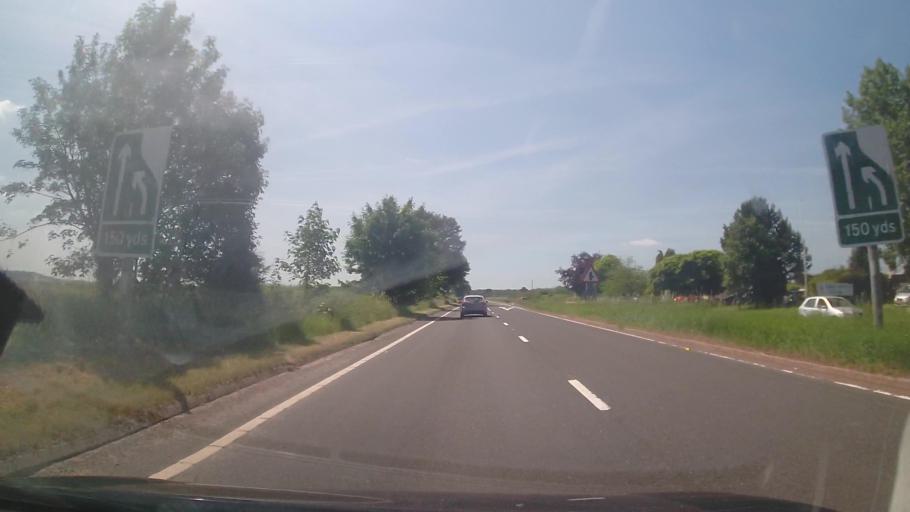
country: GB
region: England
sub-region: Herefordshire
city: Wellington
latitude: 52.1332
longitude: -2.7303
